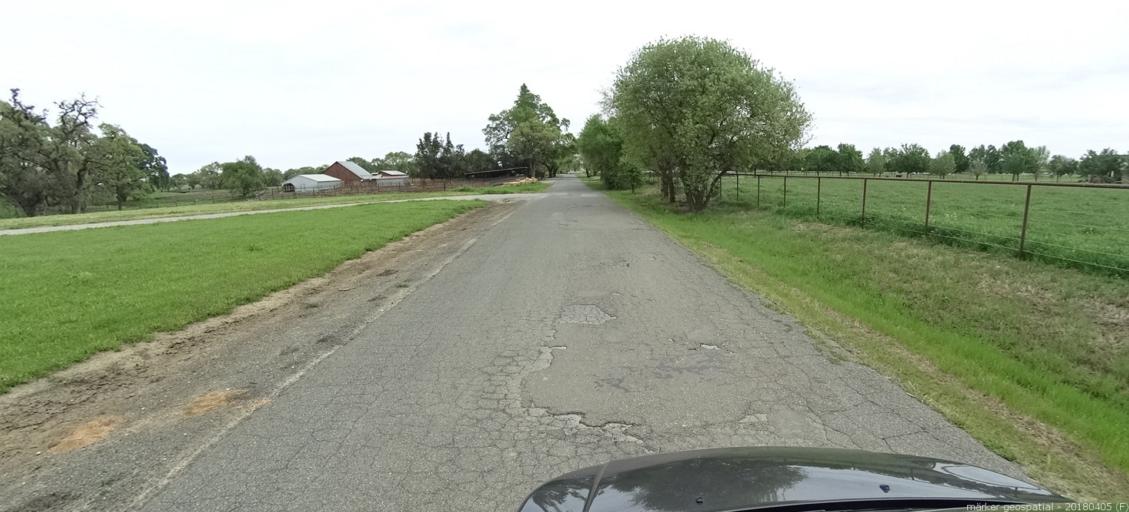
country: US
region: California
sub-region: Sacramento County
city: Galt
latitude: 38.2764
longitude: -121.3414
